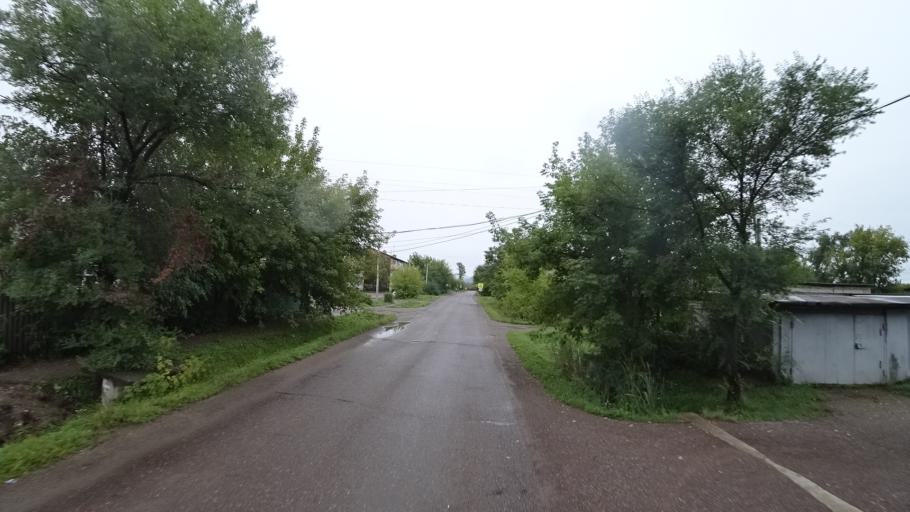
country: RU
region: Primorskiy
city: Monastyrishche
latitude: 44.2036
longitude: 132.4563
